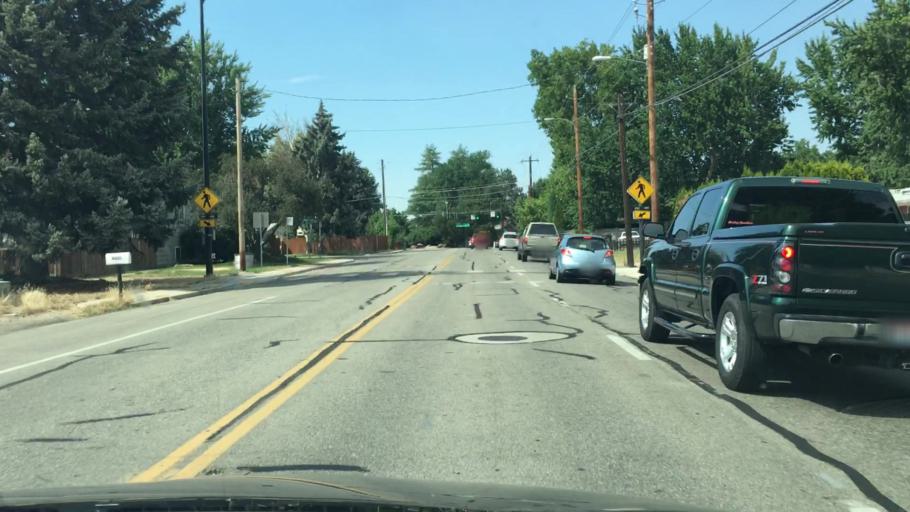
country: US
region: Idaho
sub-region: Ada County
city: Garden City
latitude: 43.6413
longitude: -116.2743
